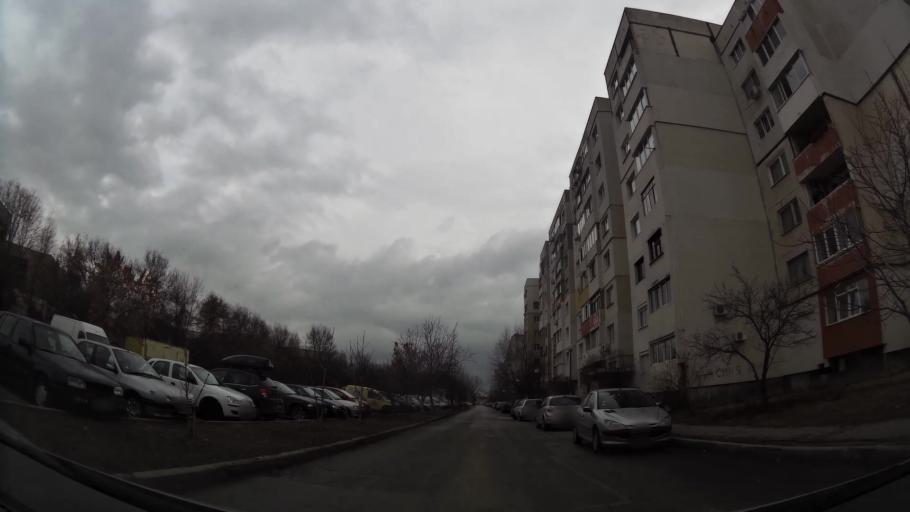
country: BG
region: Sofia-Capital
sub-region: Stolichna Obshtina
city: Sofia
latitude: 42.7381
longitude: 23.2711
